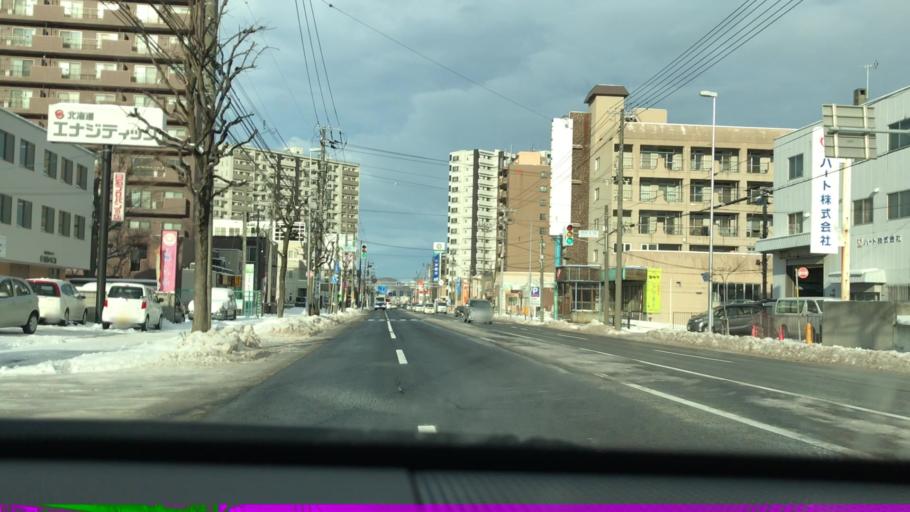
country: JP
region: Hokkaido
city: Sapporo
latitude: 43.0857
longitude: 141.2776
